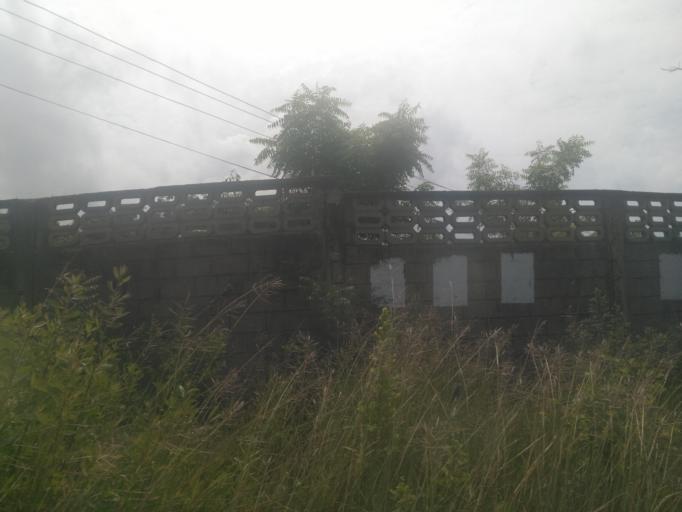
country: TZ
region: Zanzibar Urban/West
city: Zanzibar
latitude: -6.2299
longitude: 39.2118
